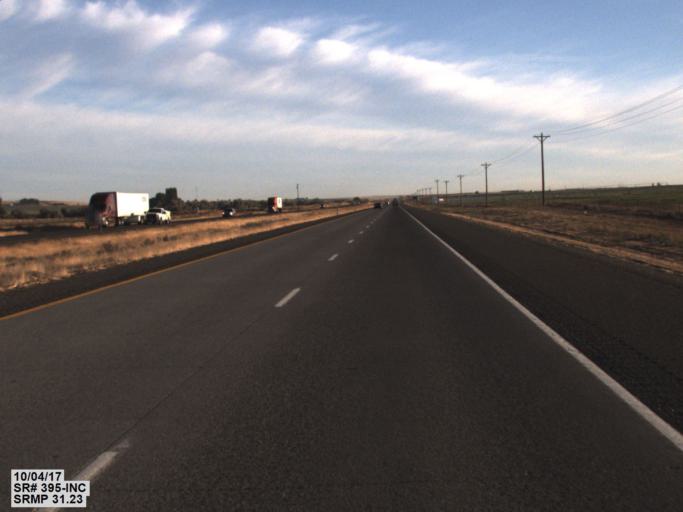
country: US
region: Washington
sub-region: Franklin County
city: Pasco
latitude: 46.3720
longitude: -119.0783
